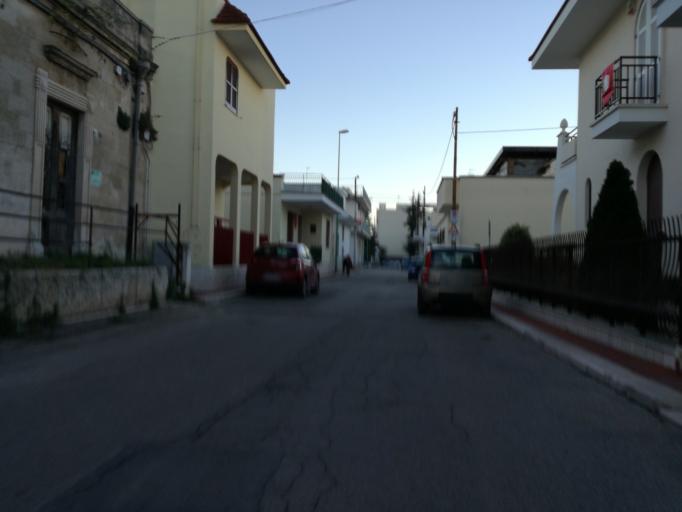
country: IT
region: Apulia
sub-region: Provincia di Bari
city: Adelfia
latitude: 41.0024
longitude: 16.8796
